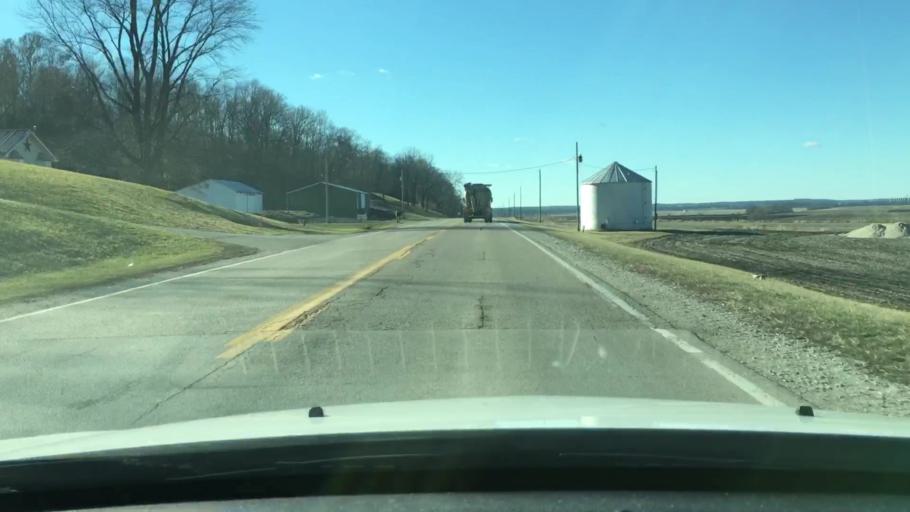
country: US
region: Illinois
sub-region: Morgan County
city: Meredosia
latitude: 39.7447
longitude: -90.5410
